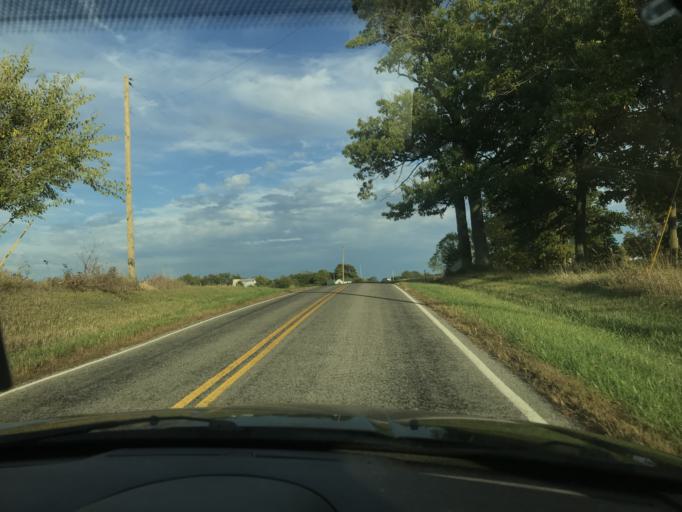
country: US
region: Ohio
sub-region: Logan County
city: West Liberty
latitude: 40.1951
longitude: -83.8035
